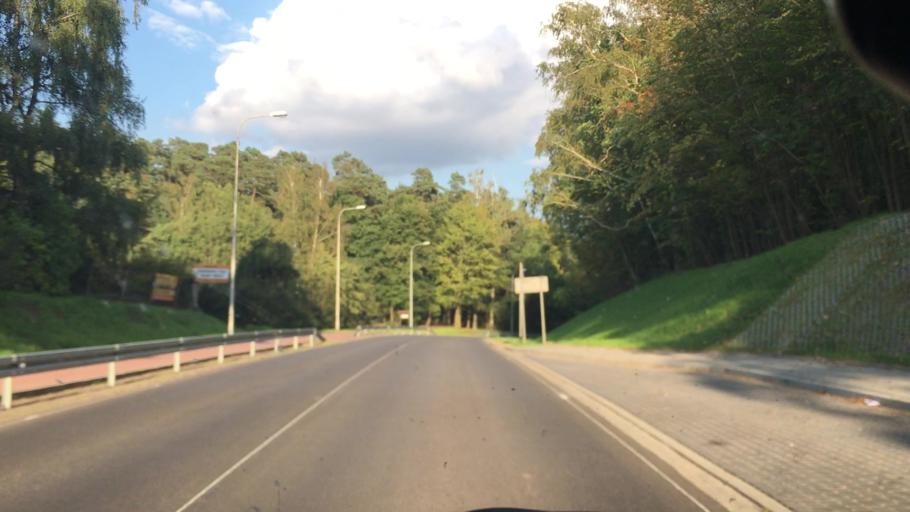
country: PL
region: Pomeranian Voivodeship
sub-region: Powiat starogardzki
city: Bobowo
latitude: 53.9285
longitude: 18.6193
